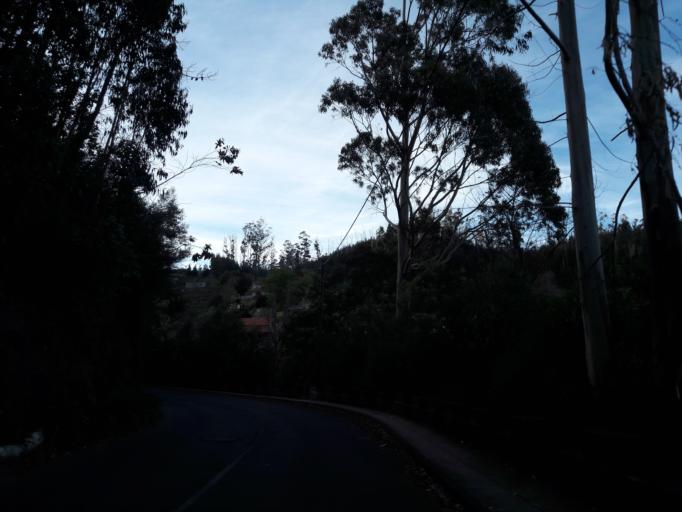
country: PT
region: Madeira
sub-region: Santa Cruz
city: Camacha
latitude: 32.6908
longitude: -16.8663
